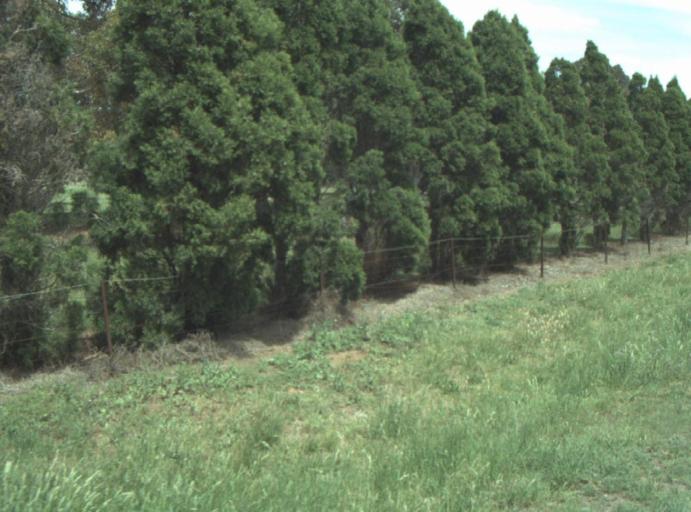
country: AU
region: Victoria
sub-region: Greater Geelong
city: Lara
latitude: -38.0250
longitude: 144.3668
